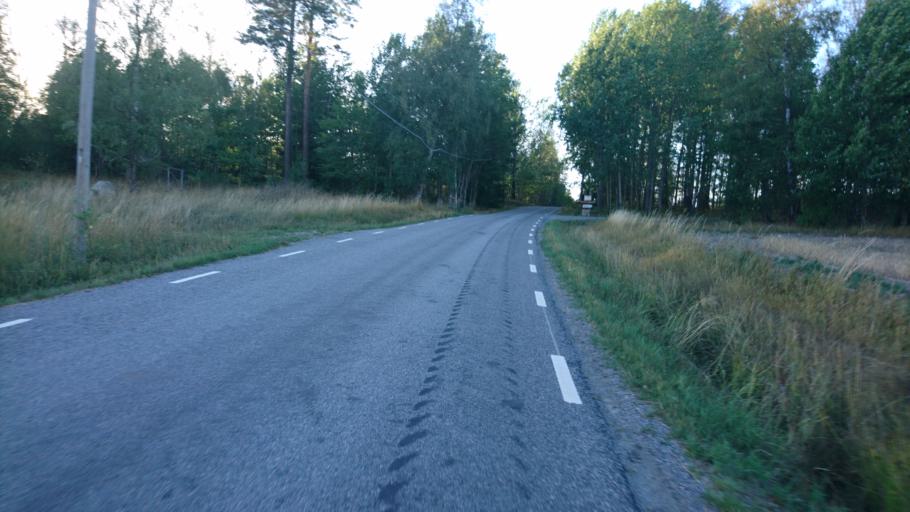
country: SE
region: Soedermanland
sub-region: Strangnas Kommun
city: Stallarholmen
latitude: 59.3951
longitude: 17.2675
